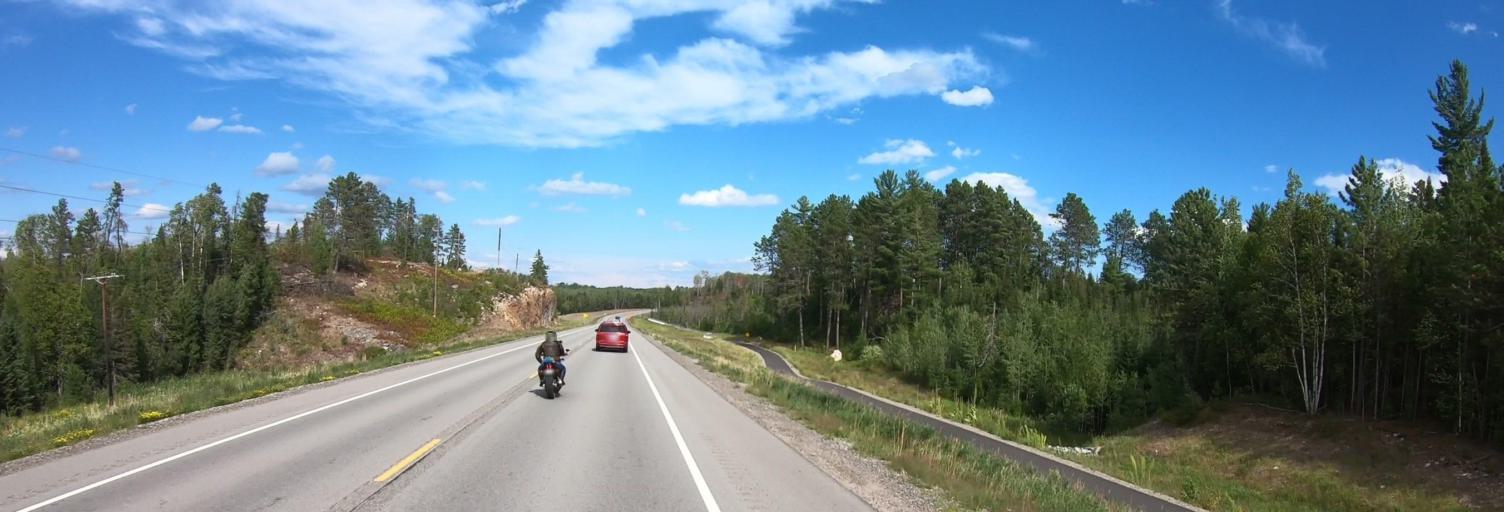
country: US
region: Minnesota
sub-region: Saint Louis County
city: Babbitt
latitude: 47.8474
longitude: -92.1197
